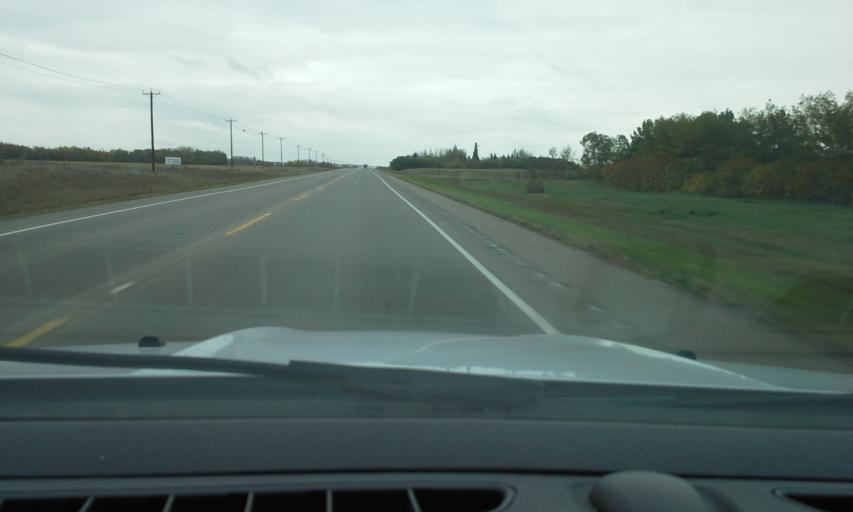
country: CA
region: Saskatchewan
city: Lloydminster
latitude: 53.2780
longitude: -109.8354
